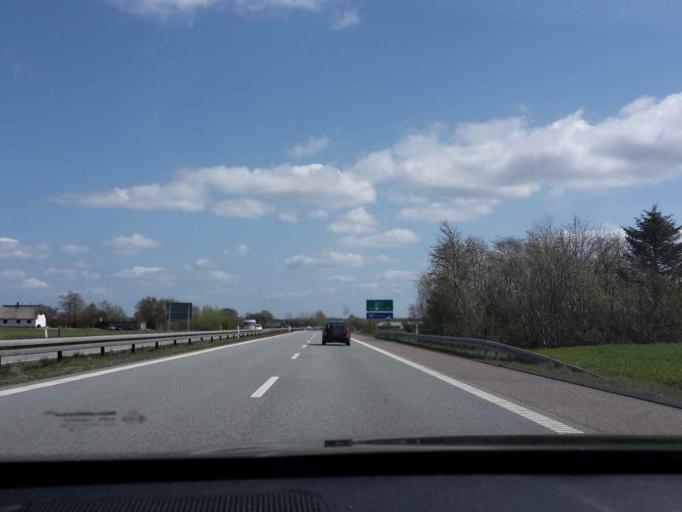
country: DK
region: South Denmark
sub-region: Vejen Kommune
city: Brorup
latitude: 55.5034
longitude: 9.0343
